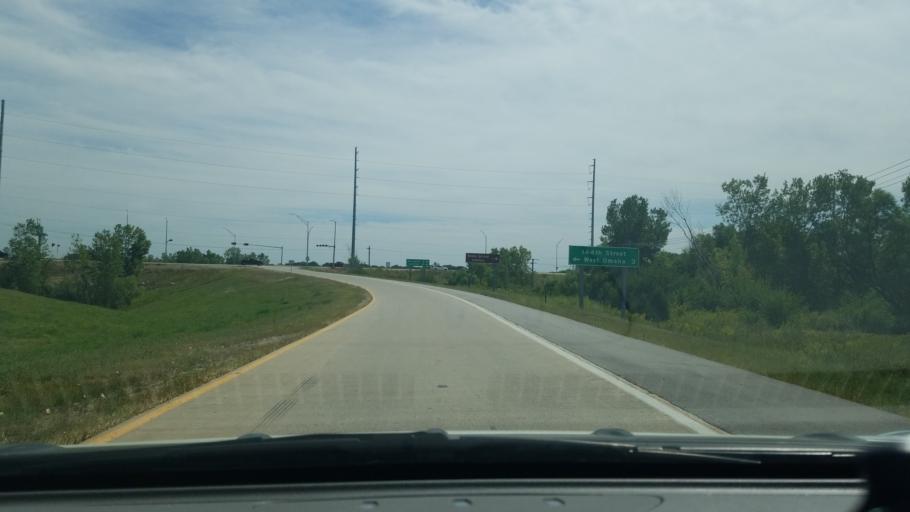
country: US
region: Nebraska
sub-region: Sarpy County
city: Chalco
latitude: 41.1467
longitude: -96.1413
